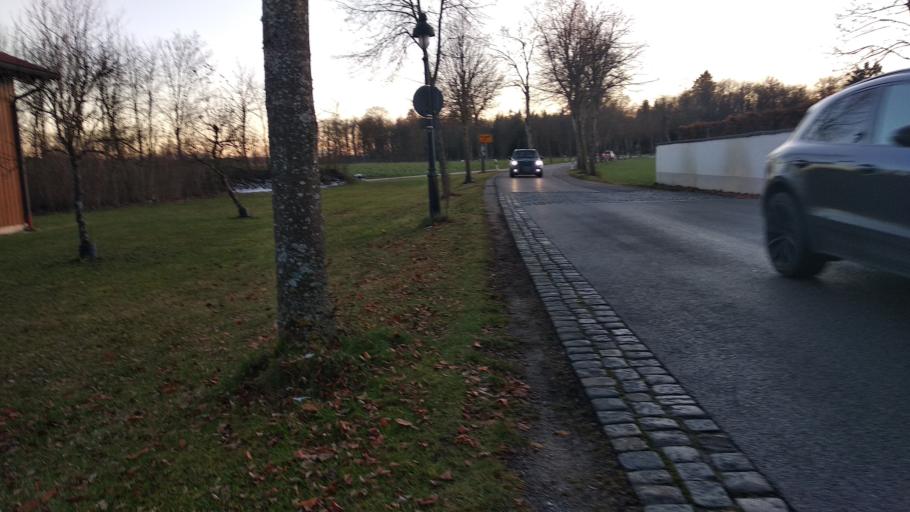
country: DE
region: Bavaria
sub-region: Upper Bavaria
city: Grasbrunn
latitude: 48.0745
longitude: 11.7737
